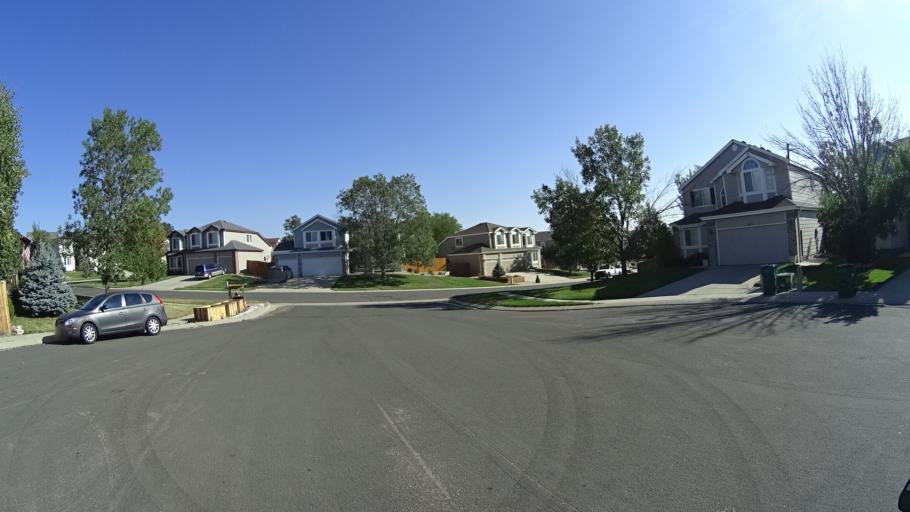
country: US
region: Colorado
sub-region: El Paso County
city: Cimarron Hills
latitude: 38.8886
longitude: -104.6995
